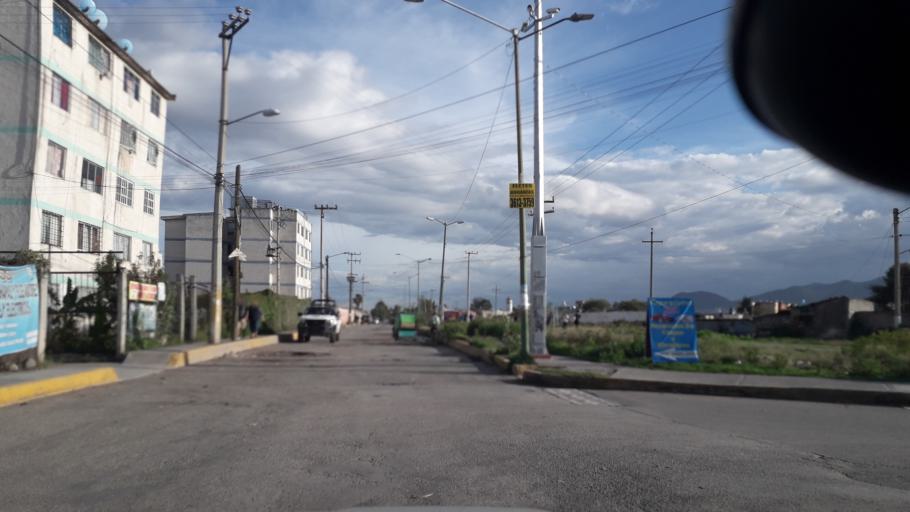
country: MX
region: Mexico
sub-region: Jaltenco
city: Alborada Jaltenco
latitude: 19.6635
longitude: -99.0723
